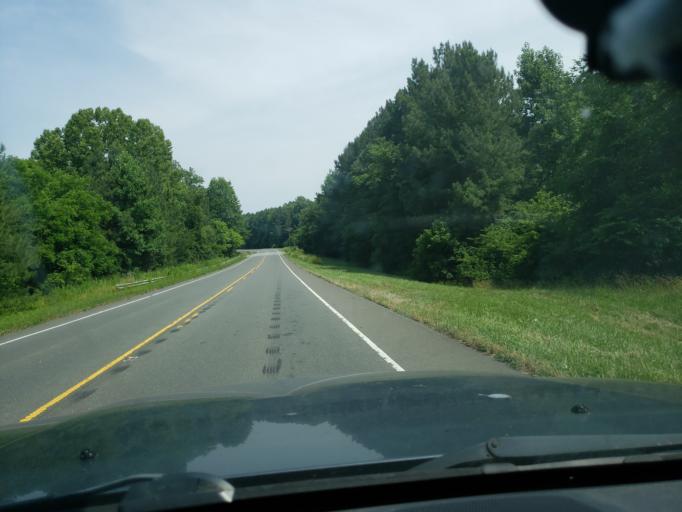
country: US
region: North Carolina
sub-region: Alamance County
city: Saxapahaw
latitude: 35.9442
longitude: -79.2467
